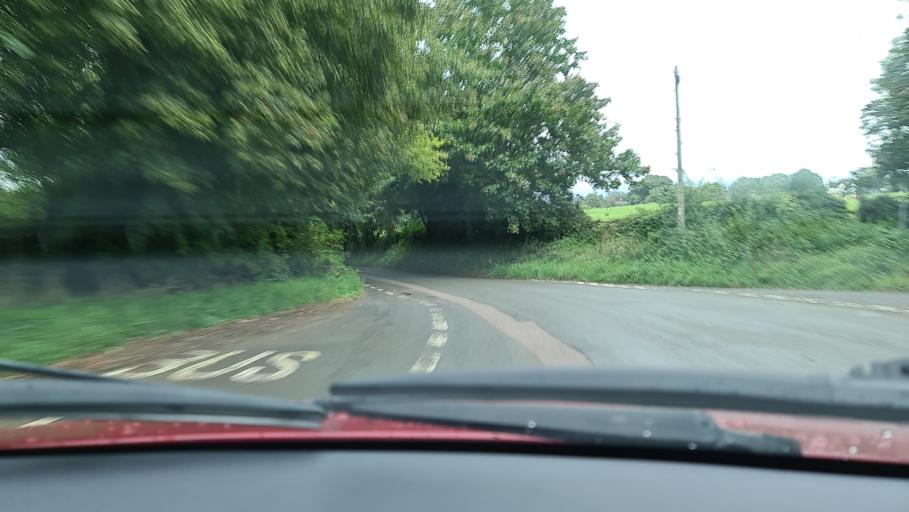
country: GB
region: England
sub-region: Oxfordshire
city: Somerton
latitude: 51.9500
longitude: -1.2773
